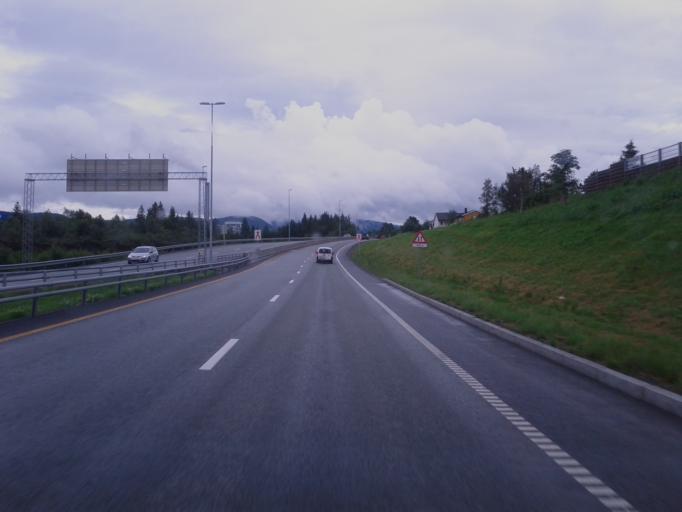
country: NO
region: Sor-Trondelag
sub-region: Trondheim
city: Trondheim
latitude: 63.3557
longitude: 10.3708
